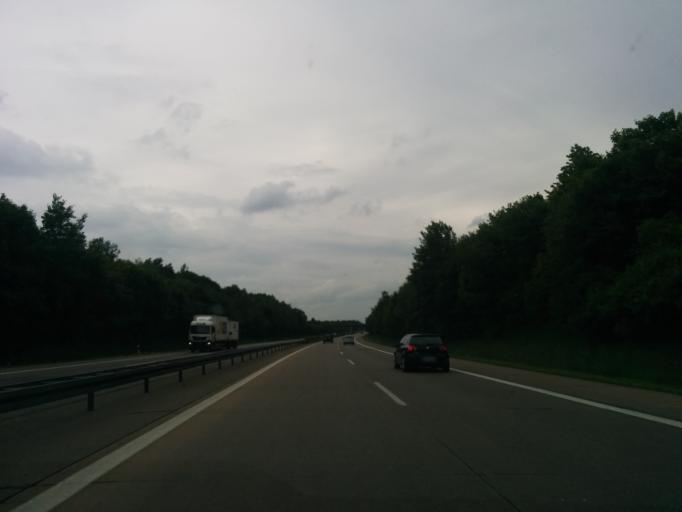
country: DE
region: Baden-Wuerttemberg
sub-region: Regierungsbezirk Stuttgart
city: Ellenberg
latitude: 49.0609
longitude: 10.1812
